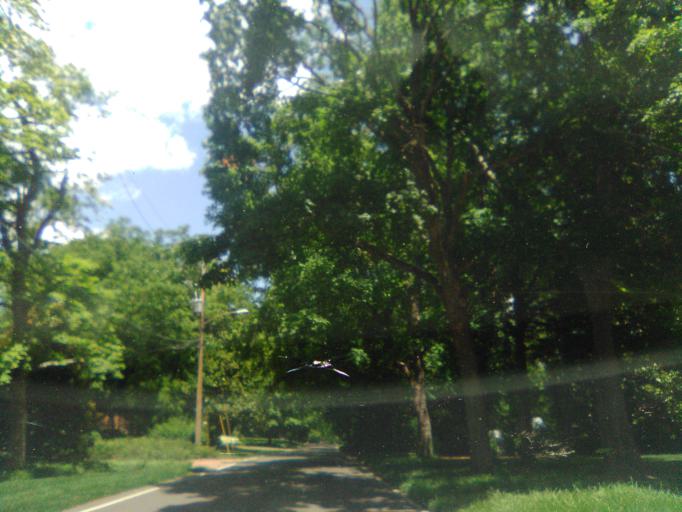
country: US
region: Tennessee
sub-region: Davidson County
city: Belle Meade
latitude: 36.1089
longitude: -86.8502
